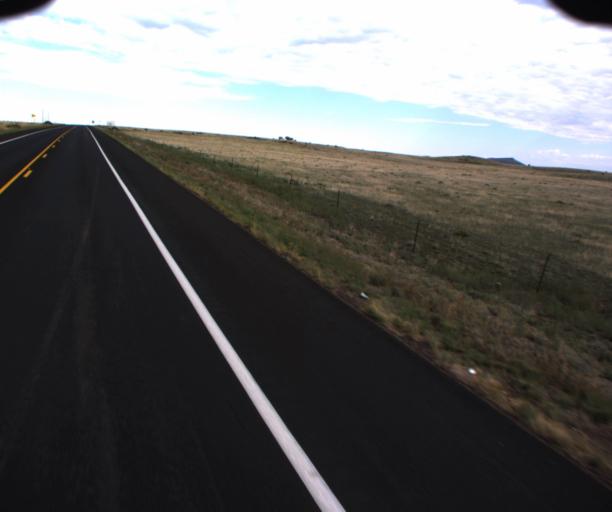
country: US
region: Arizona
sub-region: Apache County
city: Springerville
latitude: 34.1643
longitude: -109.3075
